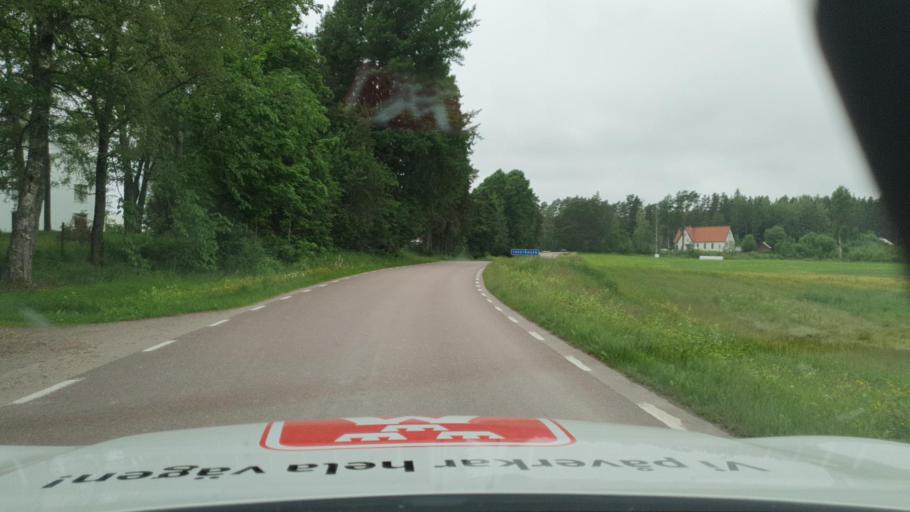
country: SE
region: Vaermland
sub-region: Kristinehamns Kommun
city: Kristinehamn
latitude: 59.4472
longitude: 13.9466
